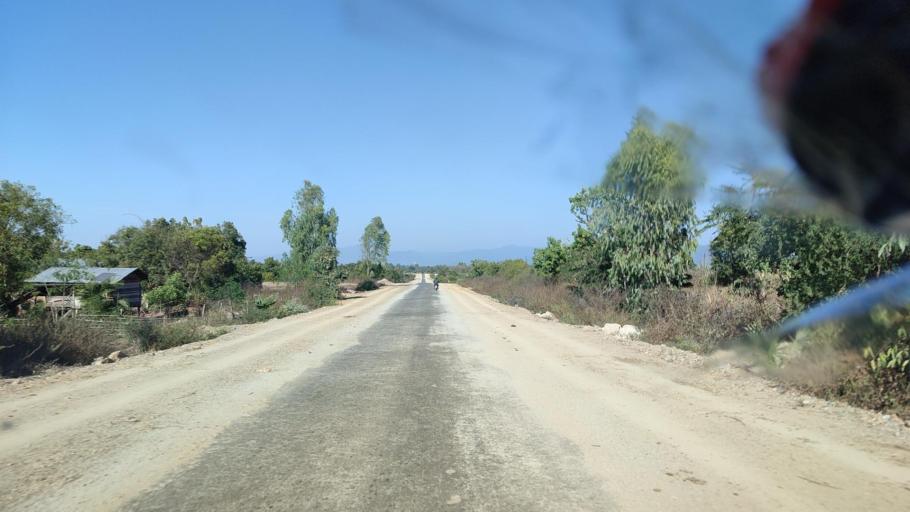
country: MM
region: Mandalay
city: Yamethin
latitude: 20.1105
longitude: 96.2688
